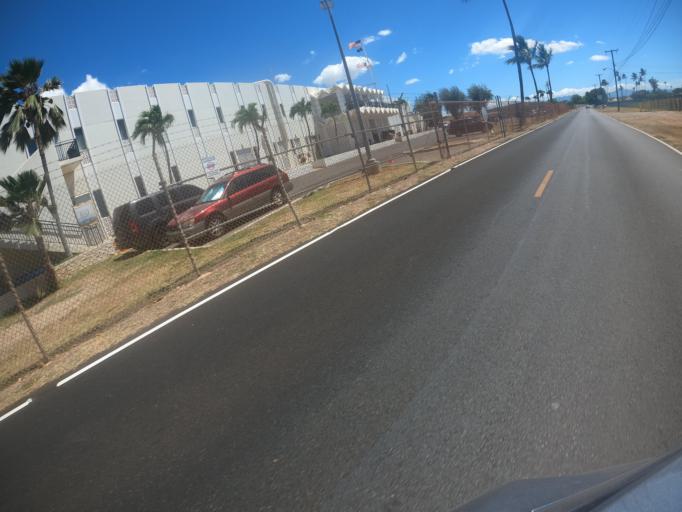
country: US
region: Hawaii
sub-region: Honolulu County
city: Makakilo City
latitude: 21.2992
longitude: -158.0708
